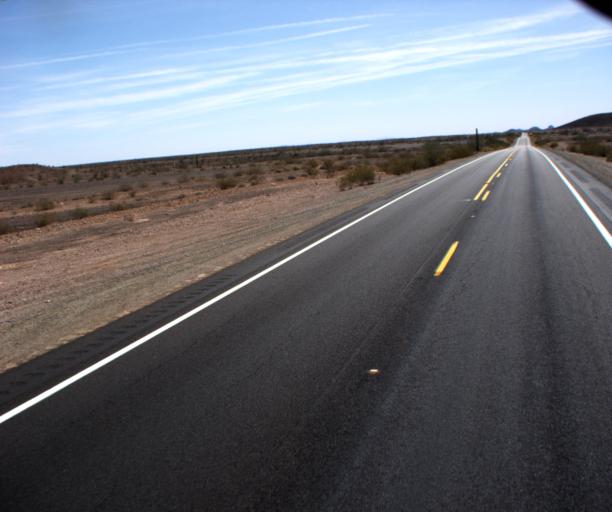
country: US
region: Arizona
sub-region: Yuma County
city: Wellton
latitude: 33.1179
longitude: -114.2930
